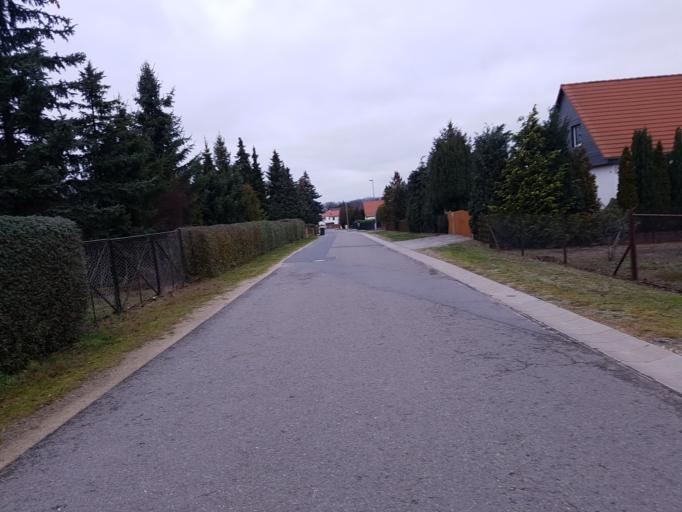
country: DE
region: Brandenburg
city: Groden
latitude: 51.4034
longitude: 13.5777
